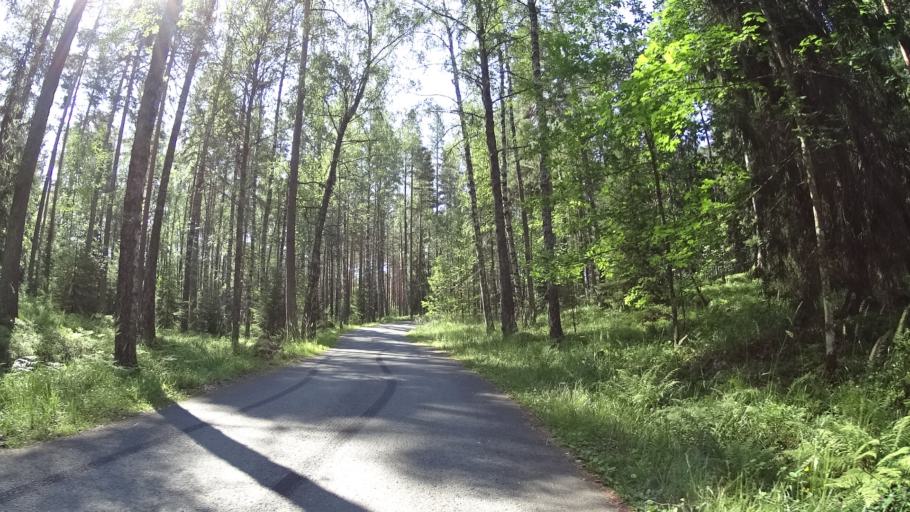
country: FI
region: Haeme
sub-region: Haemeenlinna
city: Haemeenlinna
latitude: 61.0216
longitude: 24.4621
